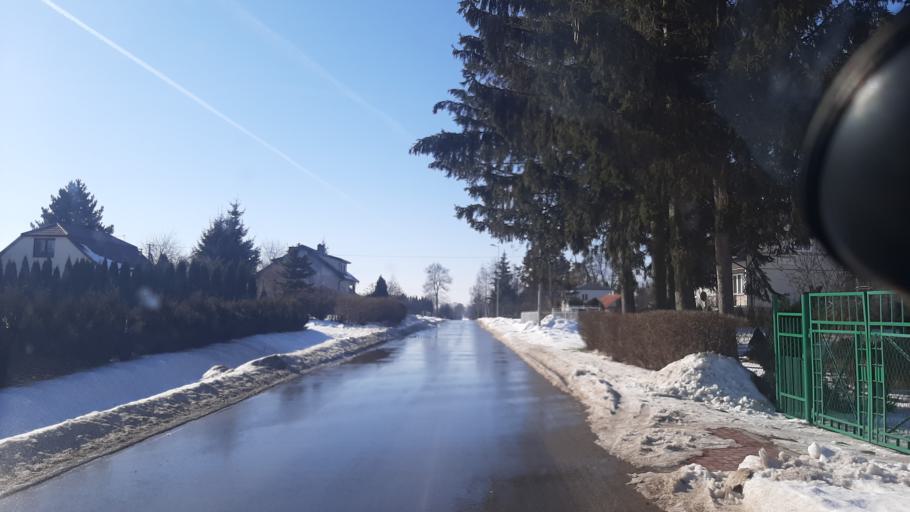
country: PL
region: Lublin Voivodeship
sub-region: Powiat lubelski
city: Garbow
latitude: 51.3175
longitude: 22.3150
